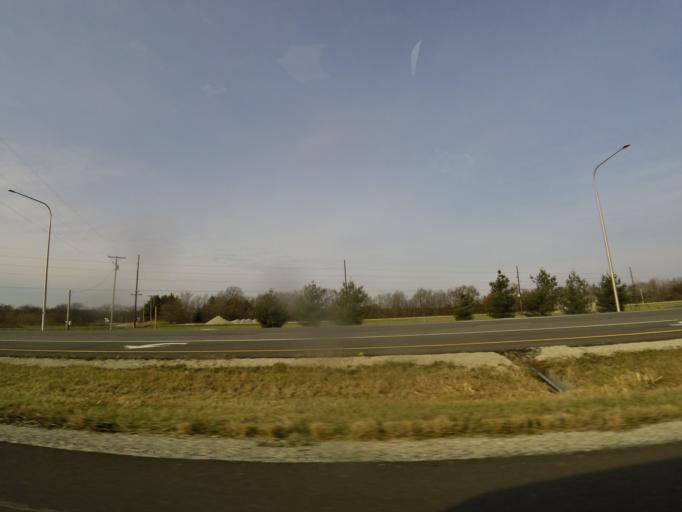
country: US
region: Illinois
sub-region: Shelby County
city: Moweaqua
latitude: 39.6105
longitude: -89.0236
